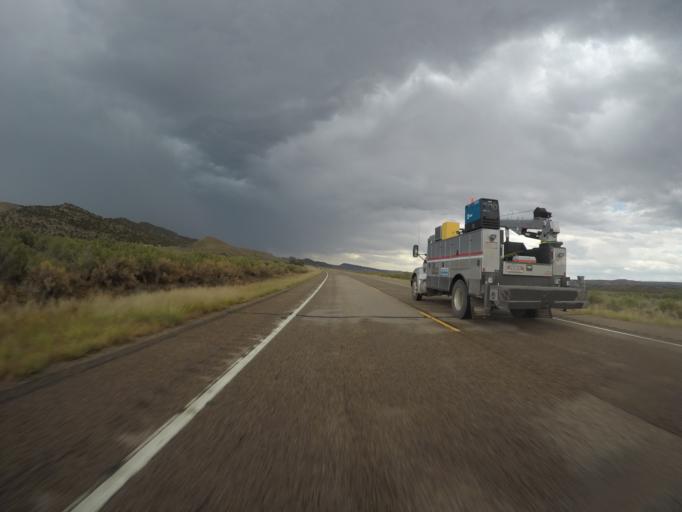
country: US
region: Colorado
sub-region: Rio Blanco County
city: Rangely
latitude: 40.2389
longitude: -108.9004
